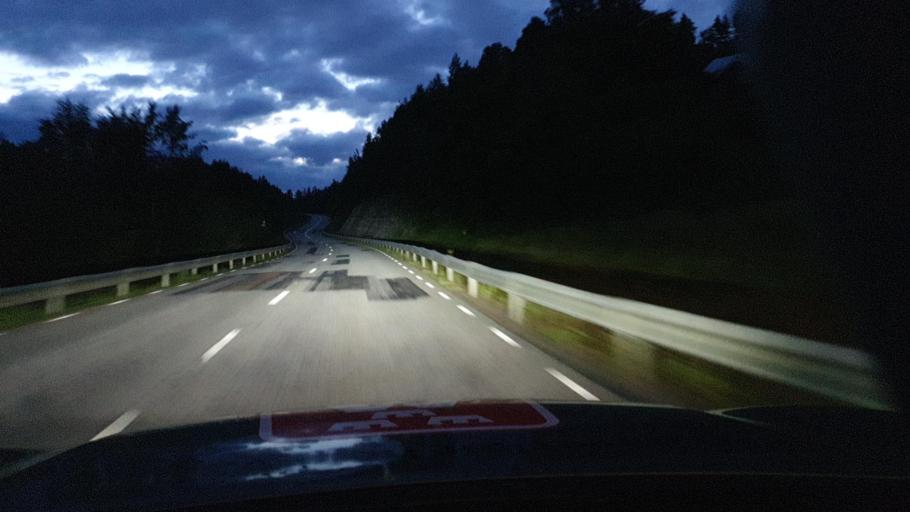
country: SE
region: OErebro
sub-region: Karlskoga Kommun
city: Karlskoga
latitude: 59.4588
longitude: 14.5033
